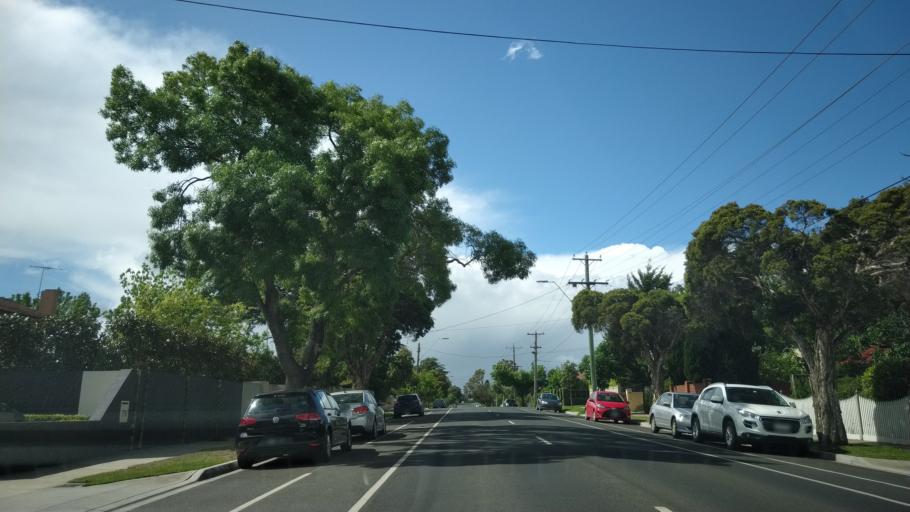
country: AU
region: Victoria
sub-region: Glen Eira
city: Caulfield
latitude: -37.8801
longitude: 145.0302
